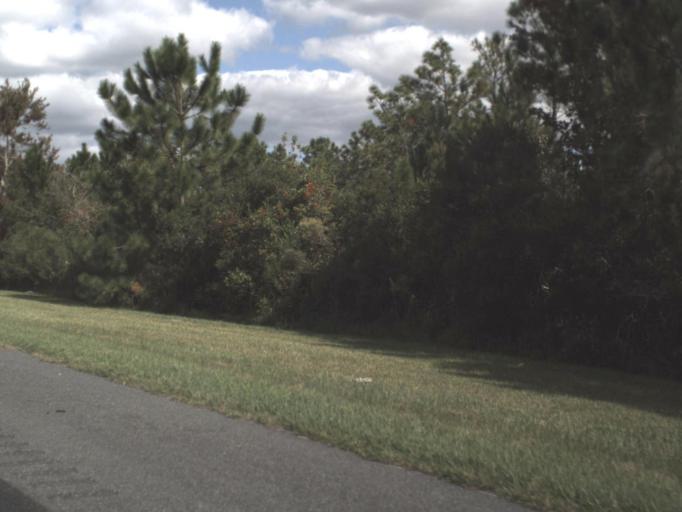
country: US
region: Florida
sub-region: Orange County
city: Southchase
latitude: 28.3849
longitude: -81.3911
